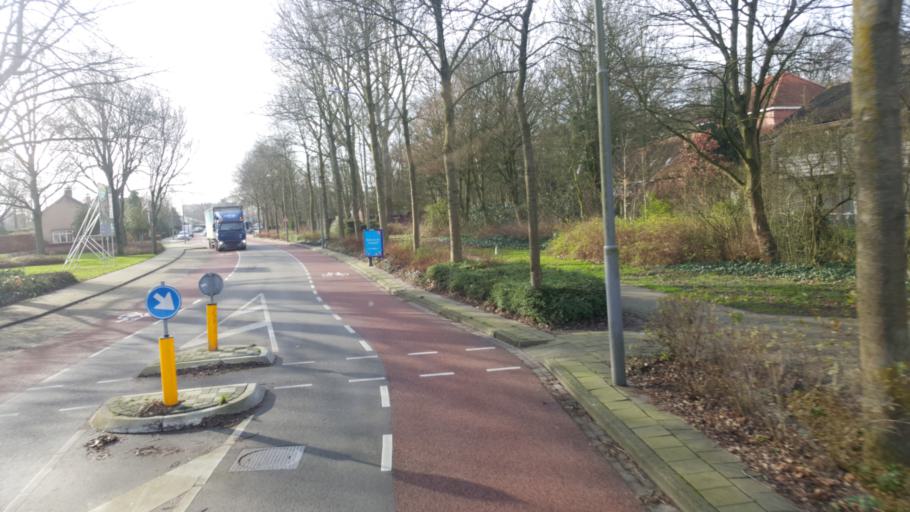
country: NL
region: North Holland
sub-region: Gemeente Heemskerk
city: Heemskerk
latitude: 52.5157
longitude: 4.6687
